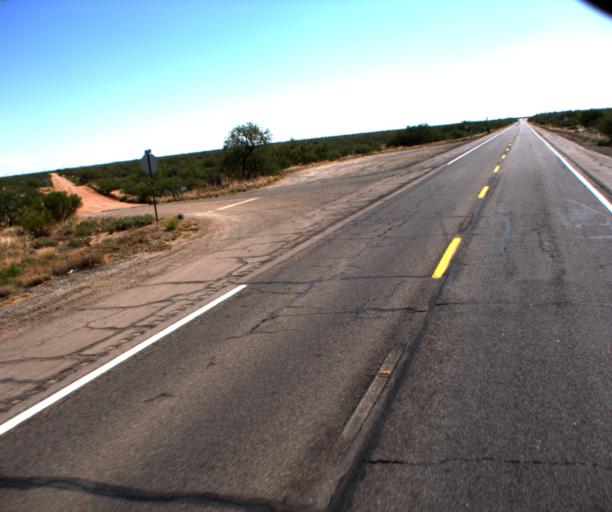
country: US
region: Arizona
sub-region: Pinal County
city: Oracle
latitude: 32.6003
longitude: -110.8721
